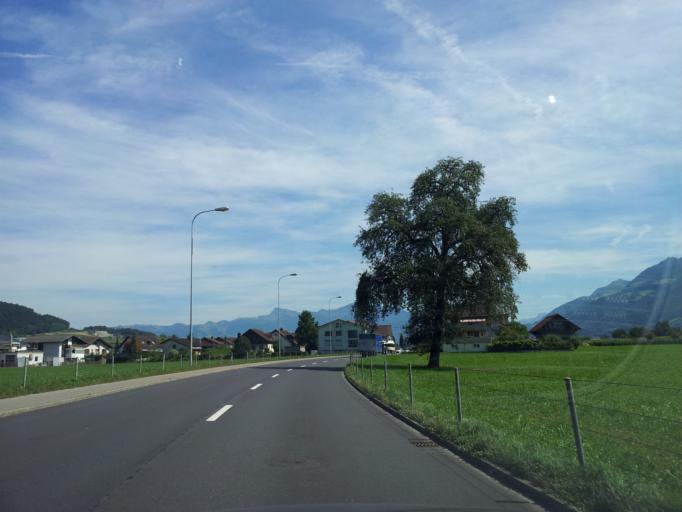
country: CH
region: Schwyz
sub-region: Bezirk March
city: Lachen
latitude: 47.1926
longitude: 8.8778
